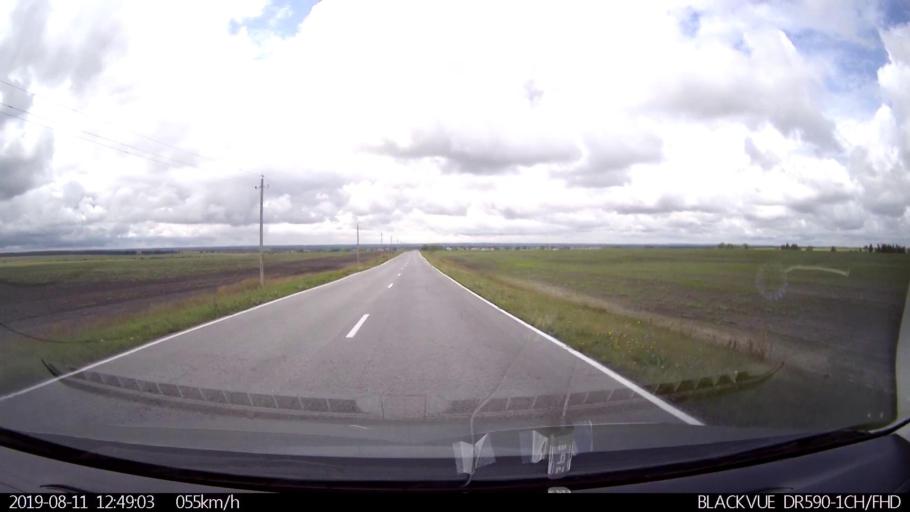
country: RU
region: Ulyanovsk
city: Ignatovka
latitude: 53.8750
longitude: 47.6932
